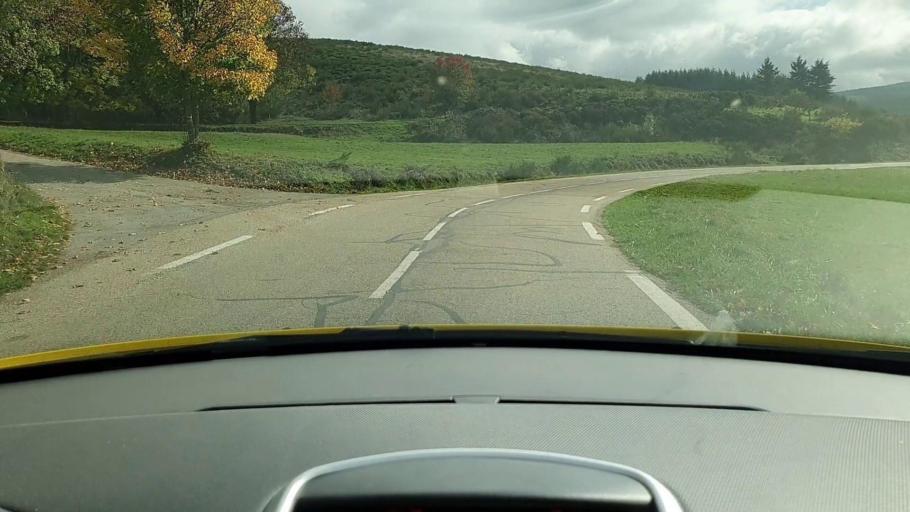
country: FR
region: Languedoc-Roussillon
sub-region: Departement de la Lozere
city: Meyrueis
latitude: 44.1212
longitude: 3.4837
